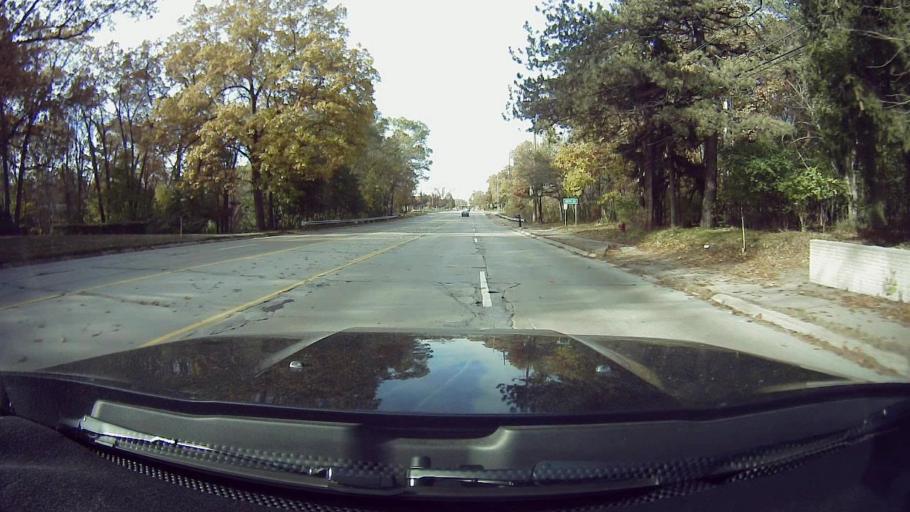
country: US
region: Michigan
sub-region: Oakland County
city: Southfield
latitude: 42.4577
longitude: -83.2710
